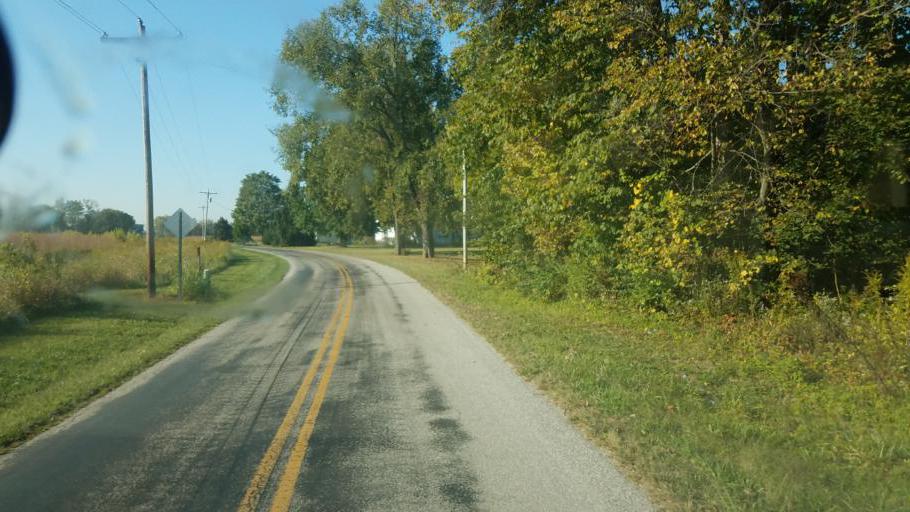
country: US
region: Ohio
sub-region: Union County
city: Richwood
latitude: 40.5570
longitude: -83.3313
